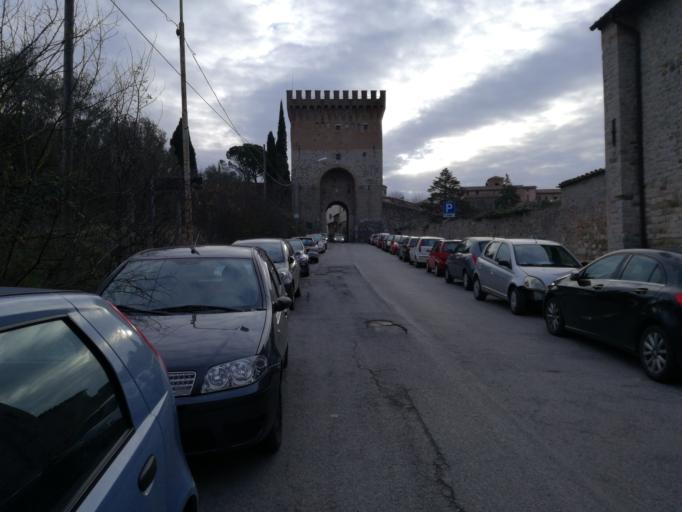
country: IT
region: Umbria
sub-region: Provincia di Perugia
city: Perugia
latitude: 43.1202
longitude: 12.3835
